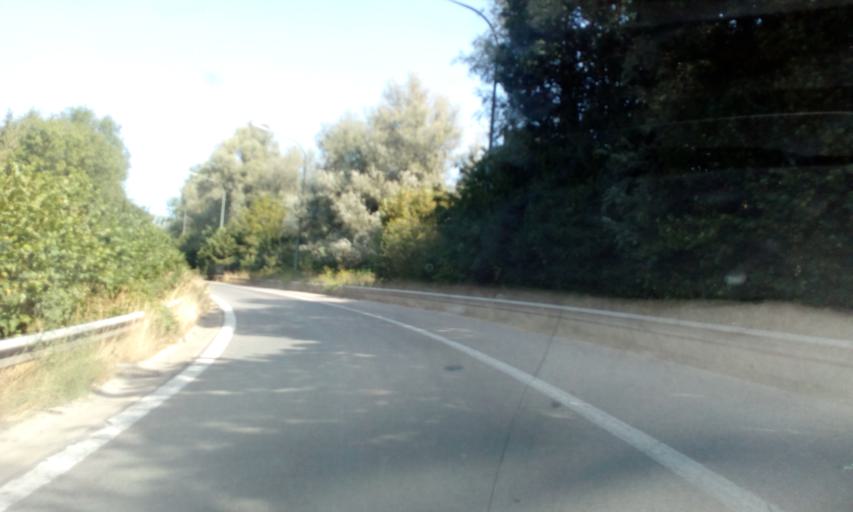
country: BE
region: Wallonia
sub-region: Province du Luxembourg
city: Aubange
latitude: 49.5527
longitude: 5.8122
